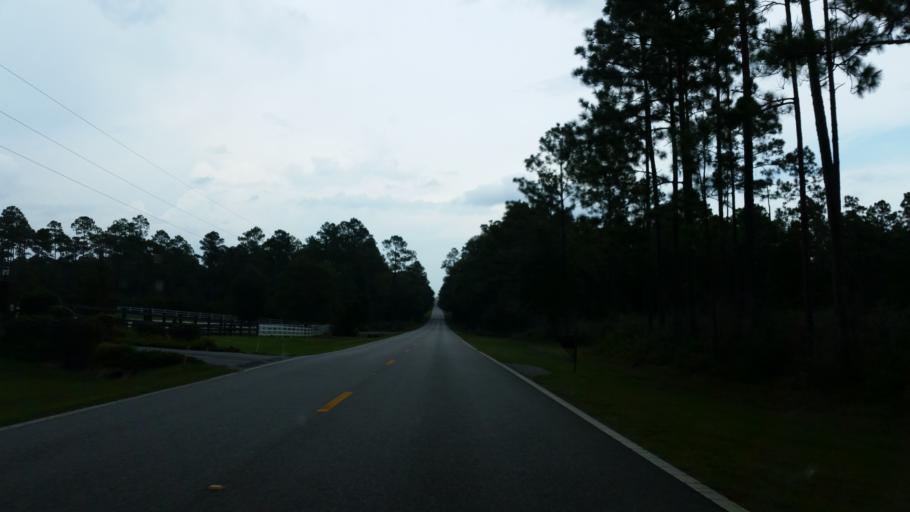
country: US
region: Florida
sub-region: Escambia County
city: Molino
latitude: 30.6814
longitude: -87.3894
